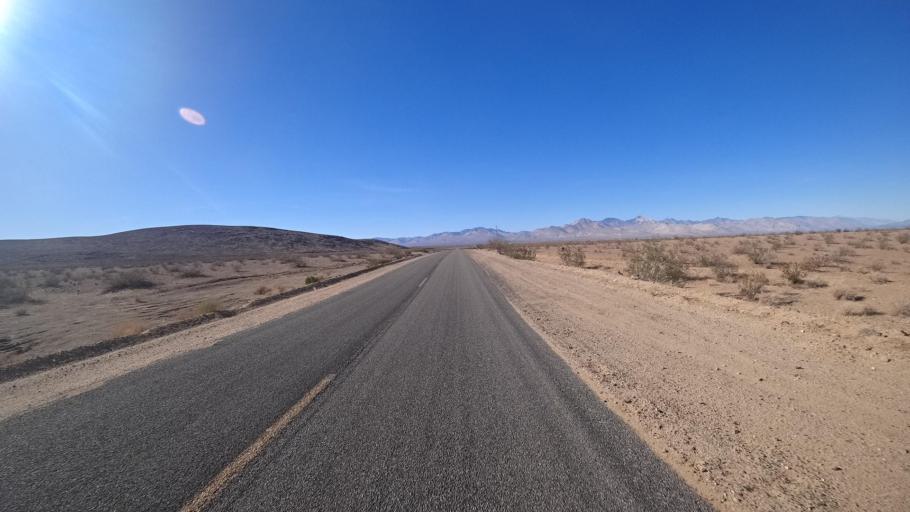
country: US
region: California
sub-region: Kern County
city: China Lake Acres
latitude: 35.5580
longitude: -117.7576
